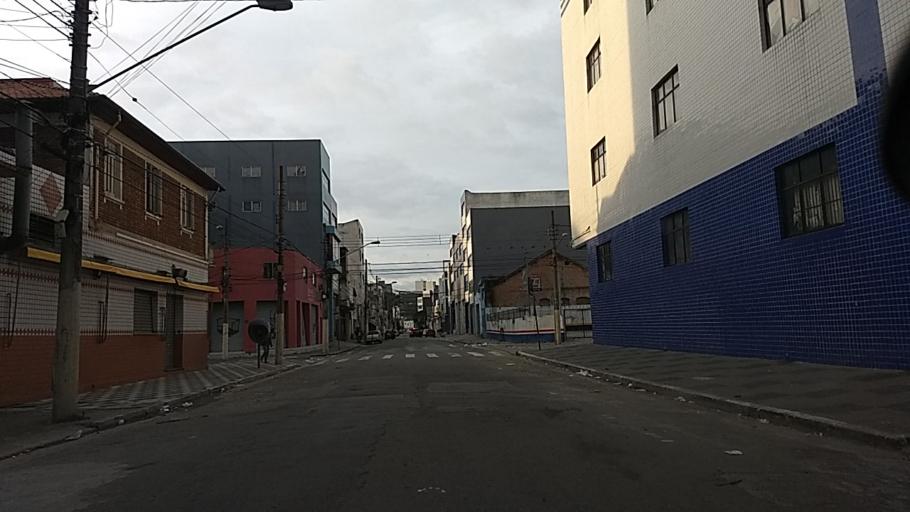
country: BR
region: Sao Paulo
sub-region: Sao Paulo
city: Sao Paulo
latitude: -23.5307
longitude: -46.6221
